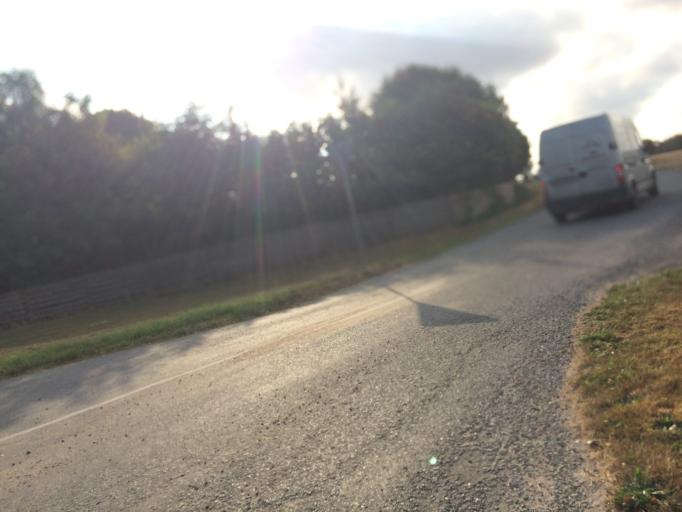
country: DK
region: Central Jutland
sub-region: Holstebro Kommune
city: Vinderup
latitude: 56.6203
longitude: 8.7403
